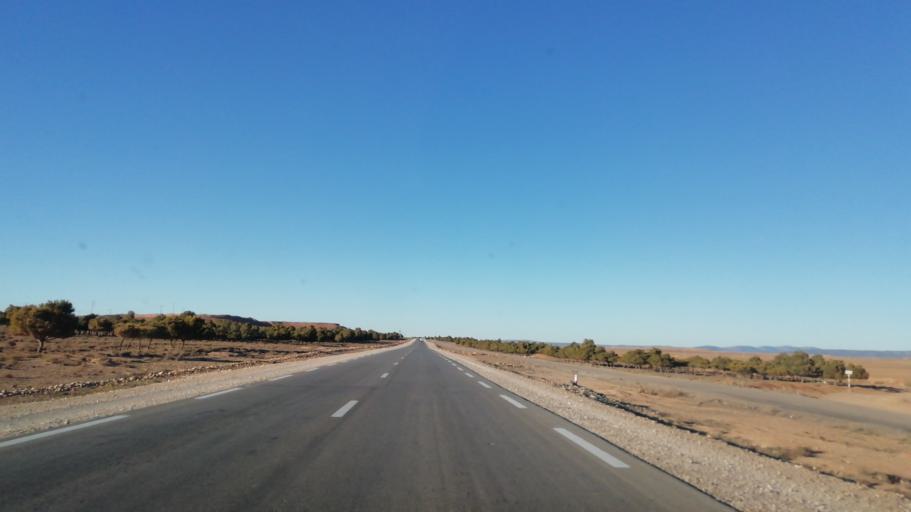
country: DZ
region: Tlemcen
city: Sebdou
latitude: 34.4938
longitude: -1.2751
